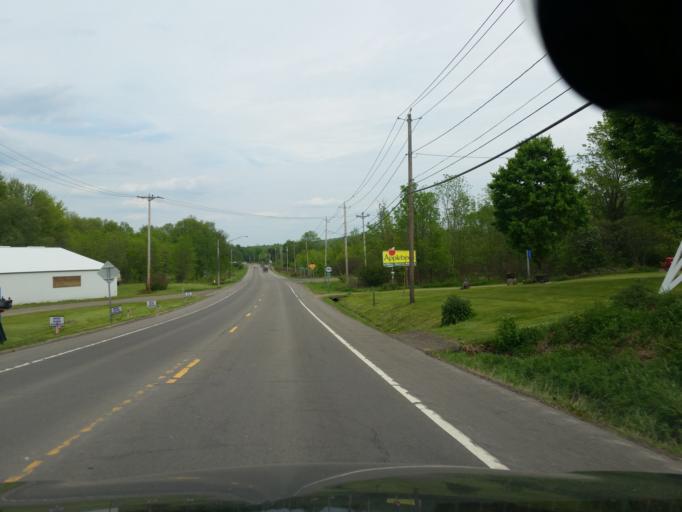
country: US
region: New York
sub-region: Chautauqua County
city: Lakewood
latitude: 42.1067
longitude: -79.3721
